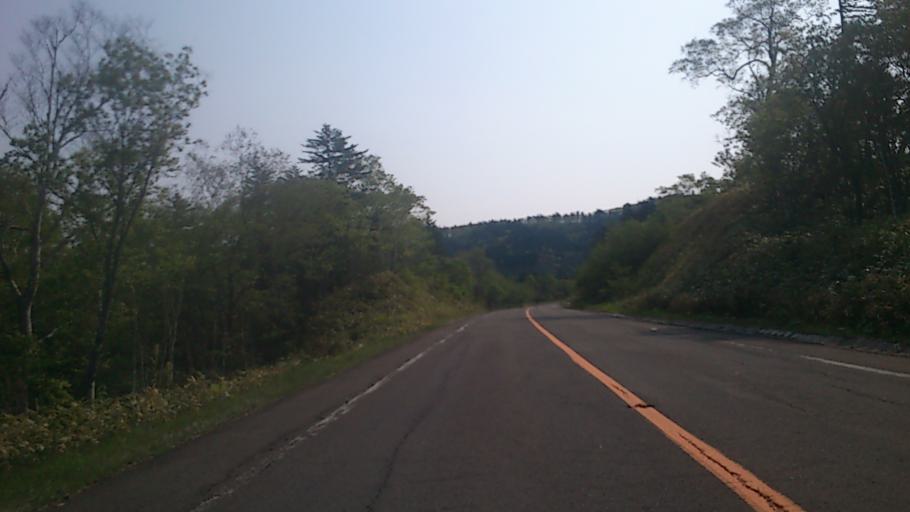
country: JP
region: Hokkaido
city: Bihoro
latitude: 43.4475
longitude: 144.2168
